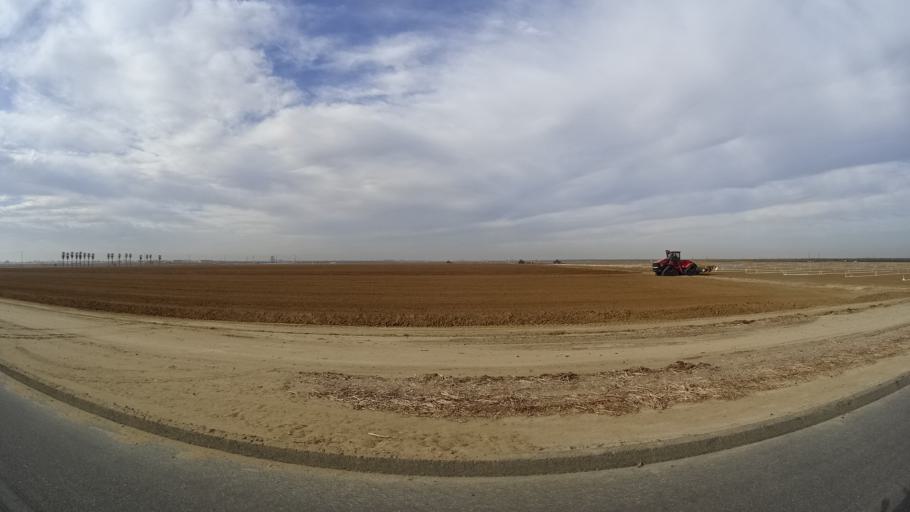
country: US
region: California
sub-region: Kern County
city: Rosedale
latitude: 35.4158
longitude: -119.1543
